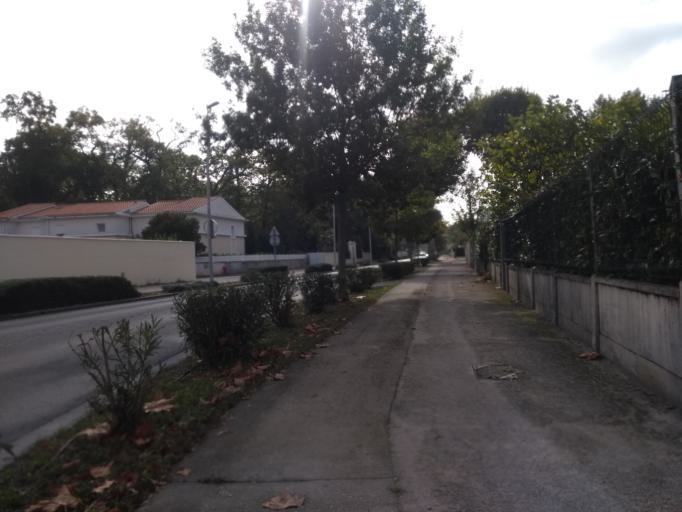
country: FR
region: Aquitaine
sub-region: Departement de la Gironde
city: Pessac
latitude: 44.7983
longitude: -0.6309
